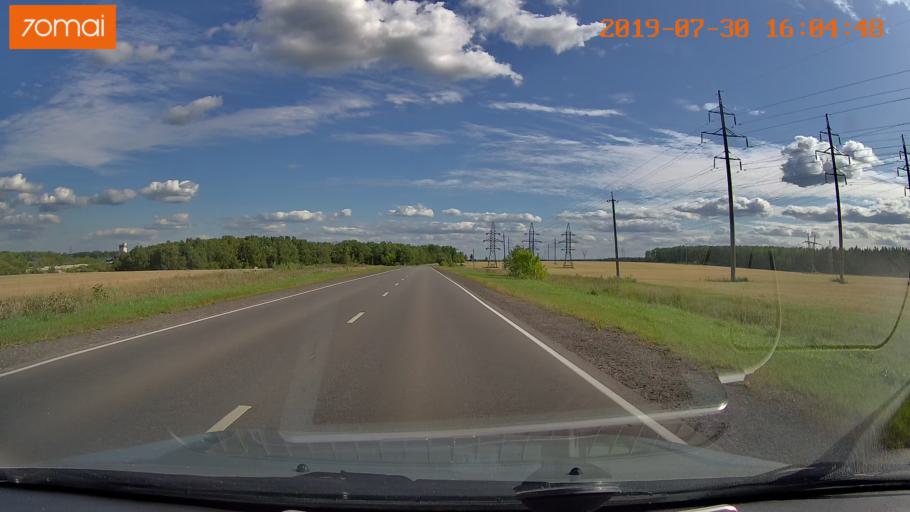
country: RU
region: Moskovskaya
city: Lopatinskiy
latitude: 55.2759
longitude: 38.7108
